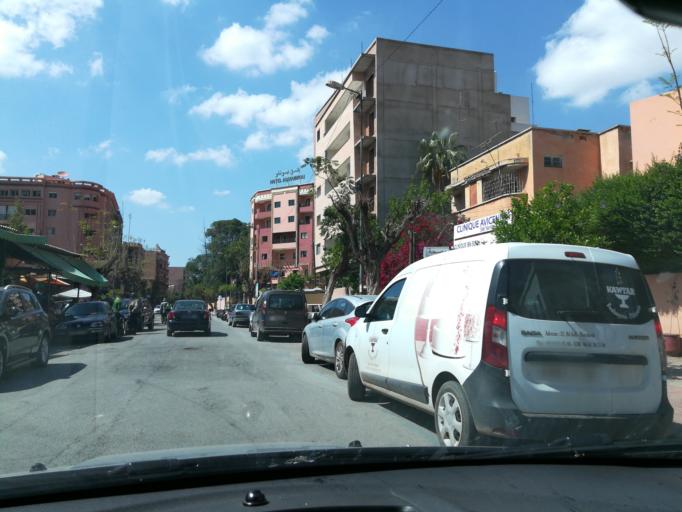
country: MA
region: Marrakech-Tensift-Al Haouz
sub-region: Marrakech
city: Marrakesh
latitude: 31.6338
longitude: -8.0063
